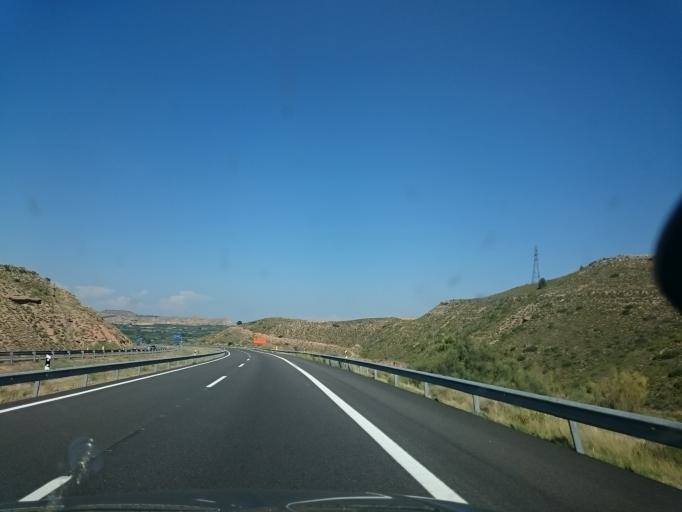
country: ES
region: Aragon
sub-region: Provincia de Huesca
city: Fraga
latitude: 41.4830
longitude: 0.3229
